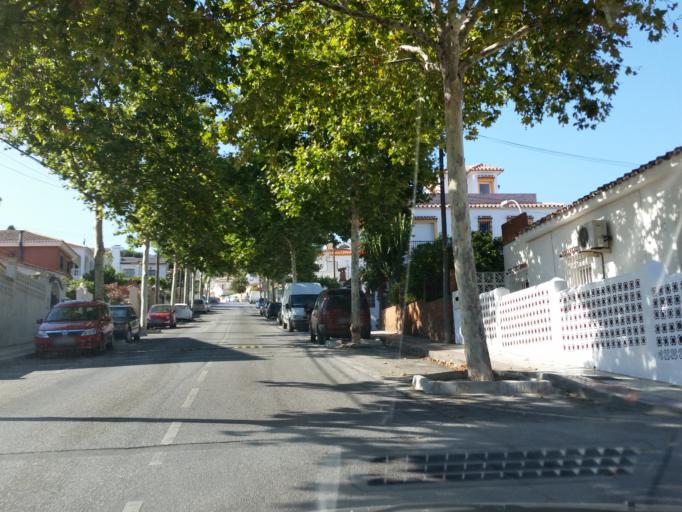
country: ES
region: Andalusia
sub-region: Provincia de Malaga
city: Benalmadena
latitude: 36.6055
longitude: -4.5347
